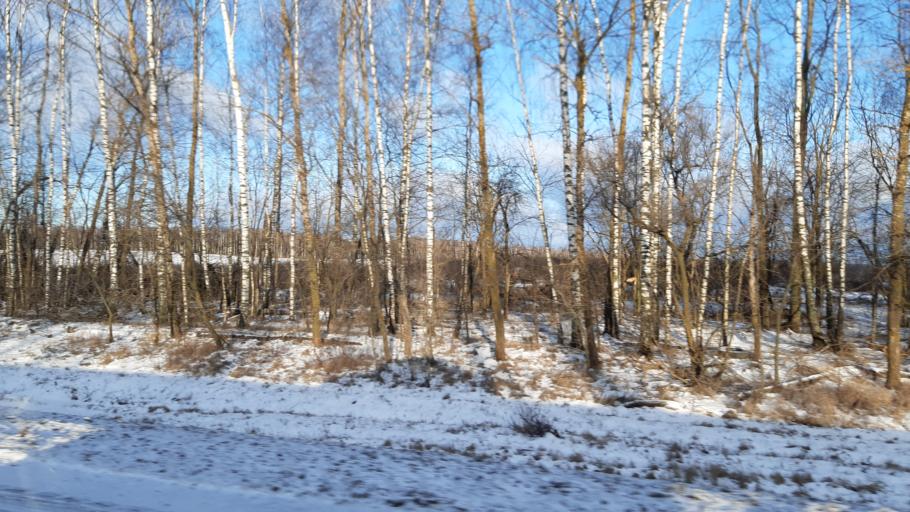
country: RU
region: Vladimir
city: Arsaki
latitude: 56.2887
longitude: 38.3877
